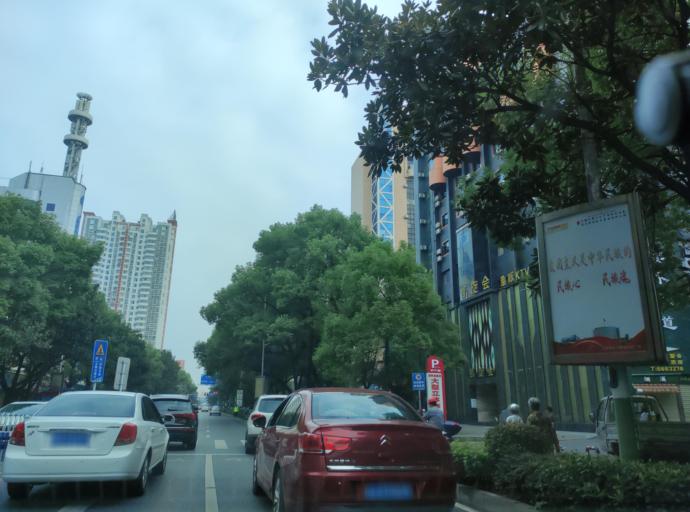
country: CN
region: Jiangxi Sheng
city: Pingxiang
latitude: 27.6426
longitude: 113.8407
